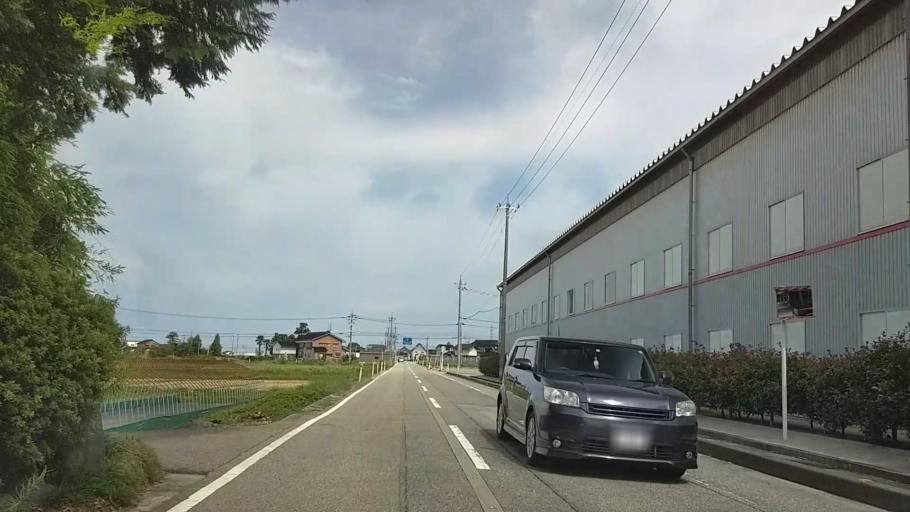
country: JP
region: Toyama
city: Kamiichi
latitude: 36.7447
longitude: 137.3736
